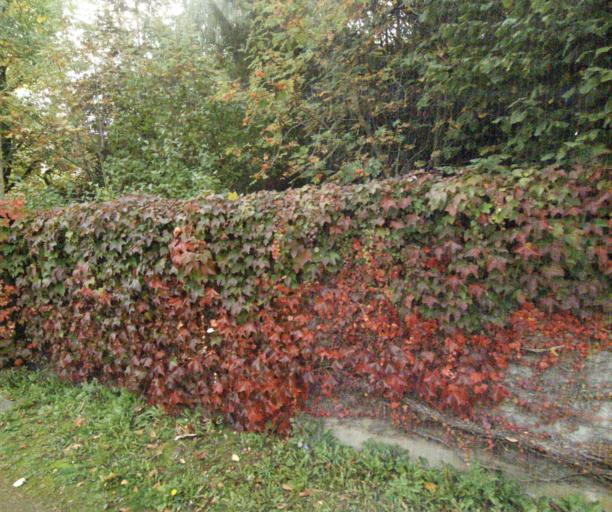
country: FR
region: Nord-Pas-de-Calais
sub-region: Departement du Nord
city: Armentieres
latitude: 50.6702
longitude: 2.8965
